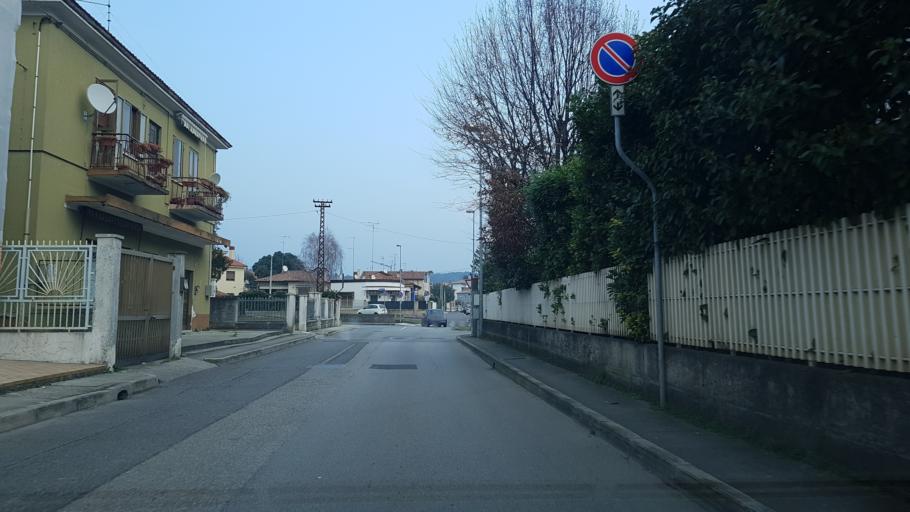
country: IT
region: Friuli Venezia Giulia
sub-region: Provincia di Gorizia
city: Monfalcone
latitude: 45.8028
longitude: 13.5241
